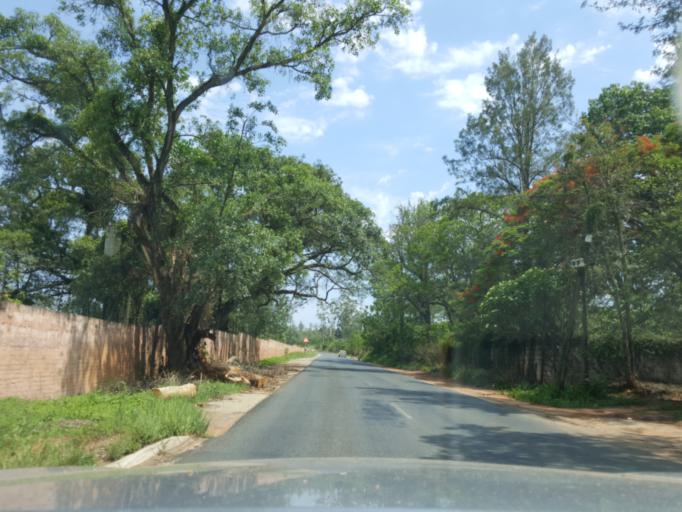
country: ZA
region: Mpumalanga
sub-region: Ehlanzeni District
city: White River
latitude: -25.3293
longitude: 31.0701
